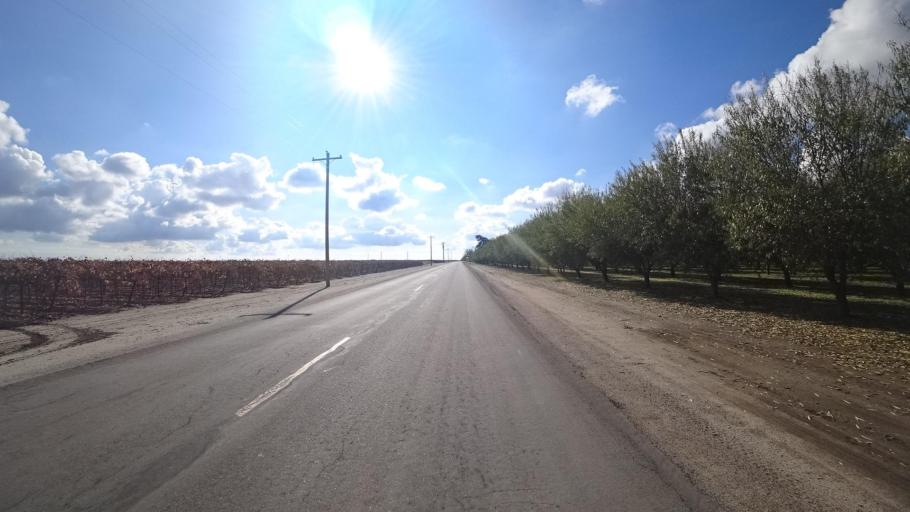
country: US
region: California
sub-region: Kern County
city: McFarland
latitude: 35.6488
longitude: -119.2322
